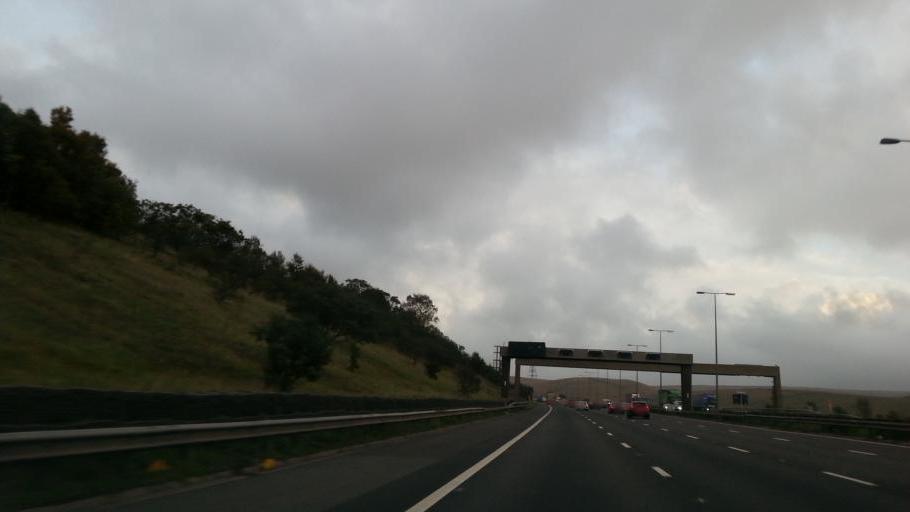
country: GB
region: England
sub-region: Borough of Rochdale
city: Littleborough
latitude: 53.6248
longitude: -2.0610
